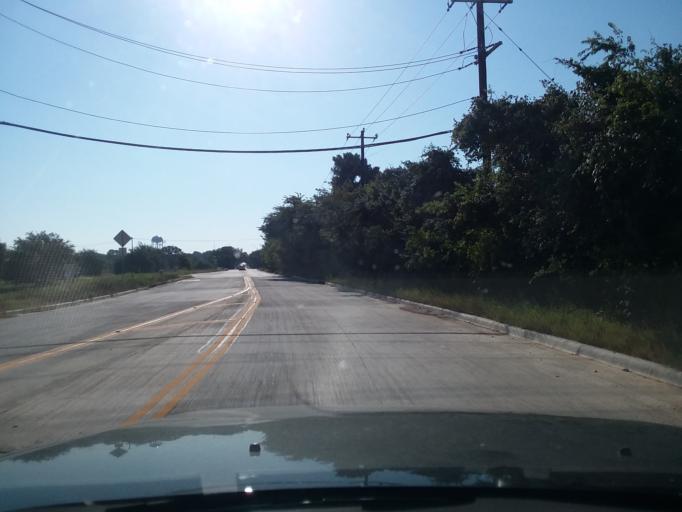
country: US
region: Texas
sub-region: Denton County
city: Double Oak
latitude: 33.0591
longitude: -97.0780
